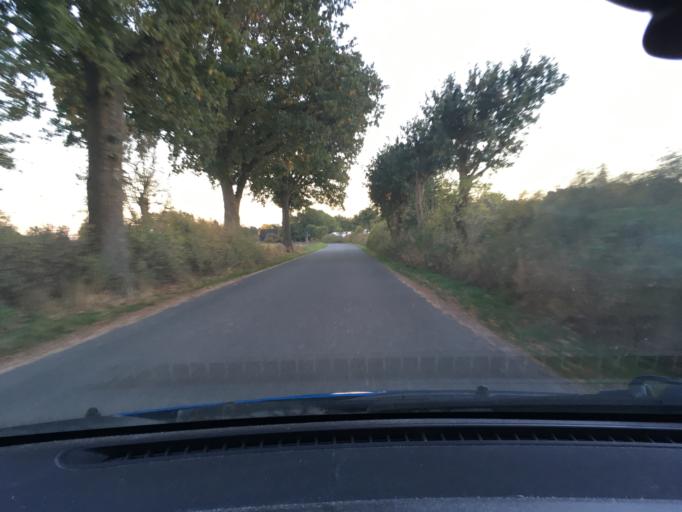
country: DE
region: Lower Saxony
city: Neetze
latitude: 53.2792
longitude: 10.6138
